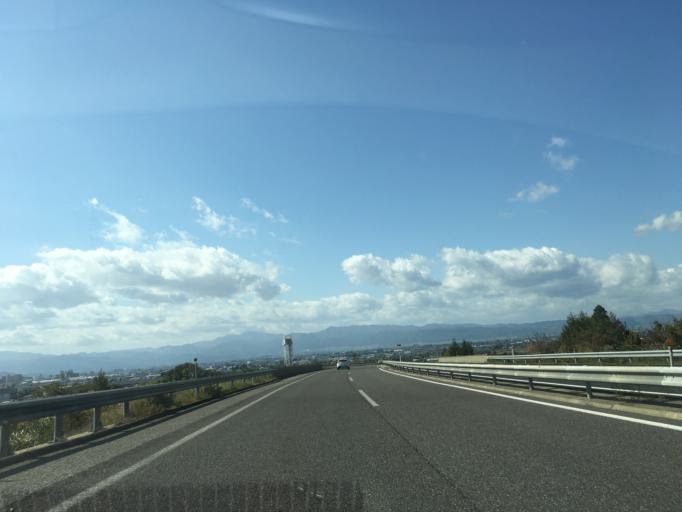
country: JP
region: Fukushima
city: Kitakata
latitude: 37.5300
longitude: 139.9494
